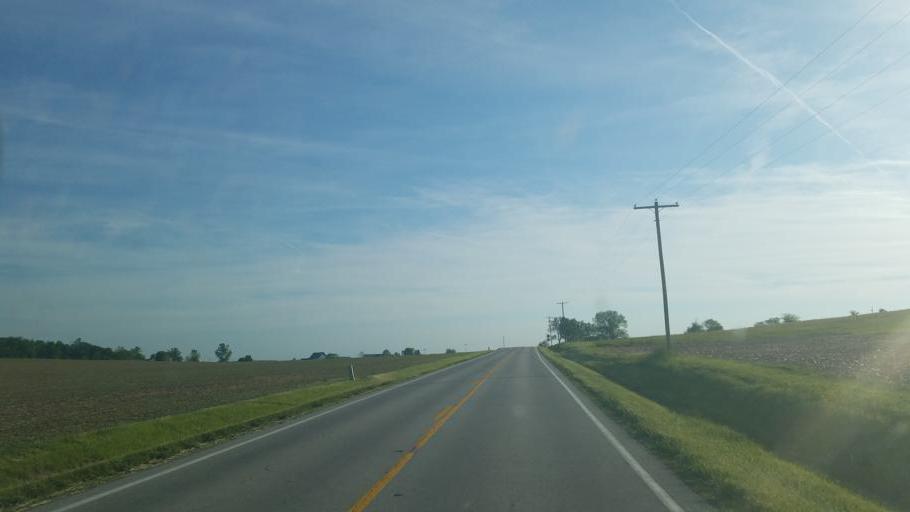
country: US
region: Ohio
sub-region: Highland County
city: Greenfield
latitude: 39.3960
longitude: -83.3200
